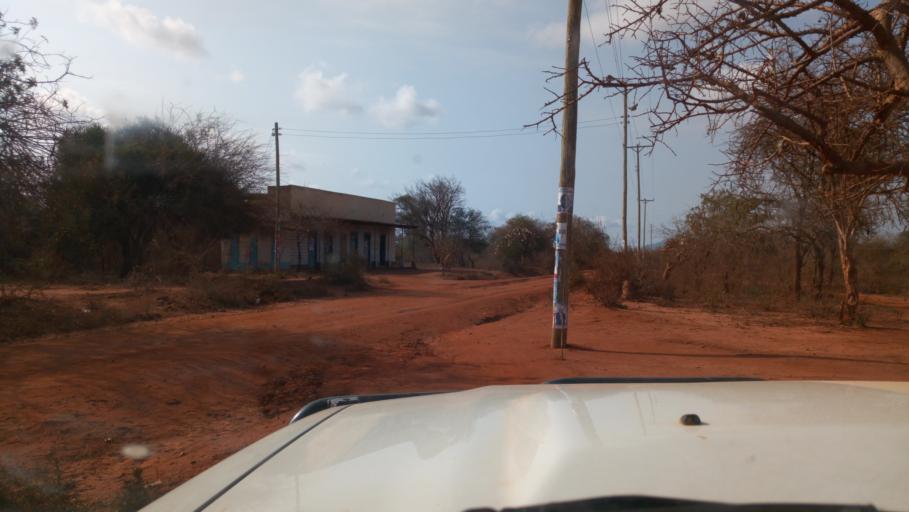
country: KE
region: Kitui
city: Kitui
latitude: -1.9050
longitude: 38.2486
